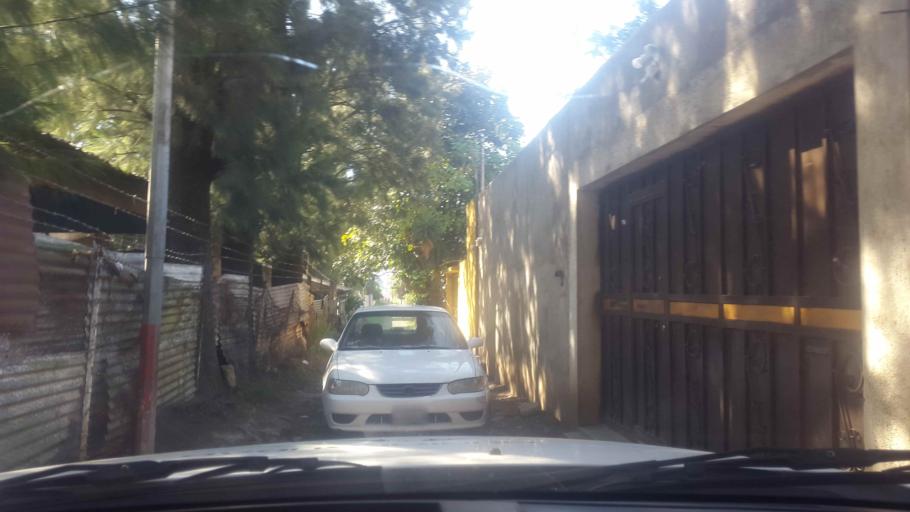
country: GT
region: Guatemala
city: Petapa
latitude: 14.5130
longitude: -90.5392
